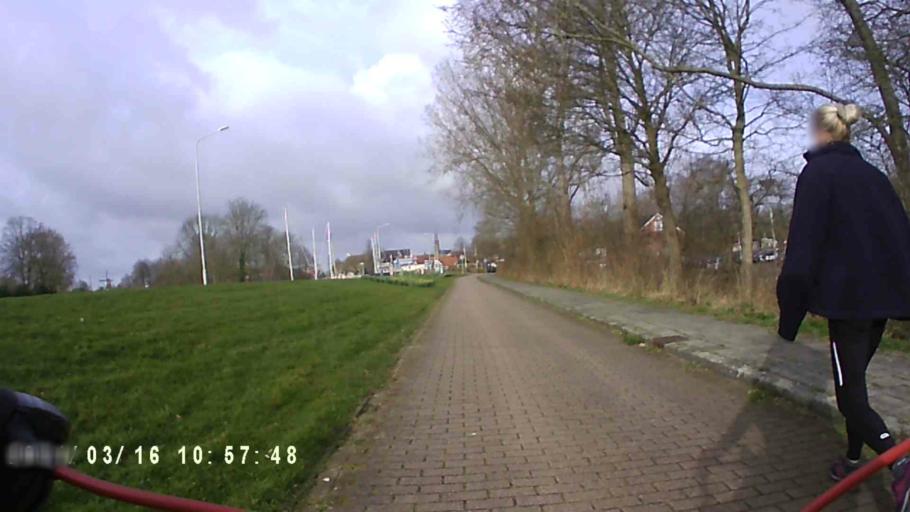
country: NL
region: Friesland
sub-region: Gemeente Dongeradeel
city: Dokkum
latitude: 53.3259
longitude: 6.0061
